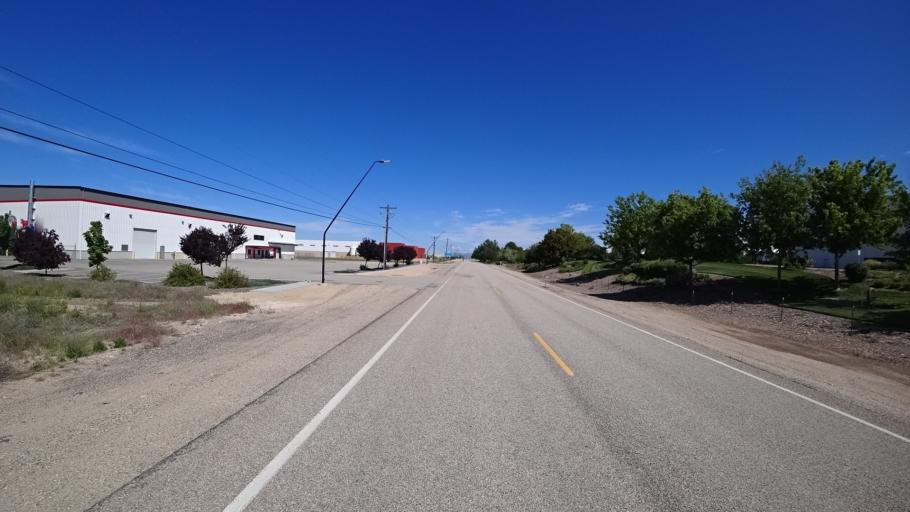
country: US
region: Idaho
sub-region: Ada County
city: Boise
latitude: 43.5225
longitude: -116.1475
